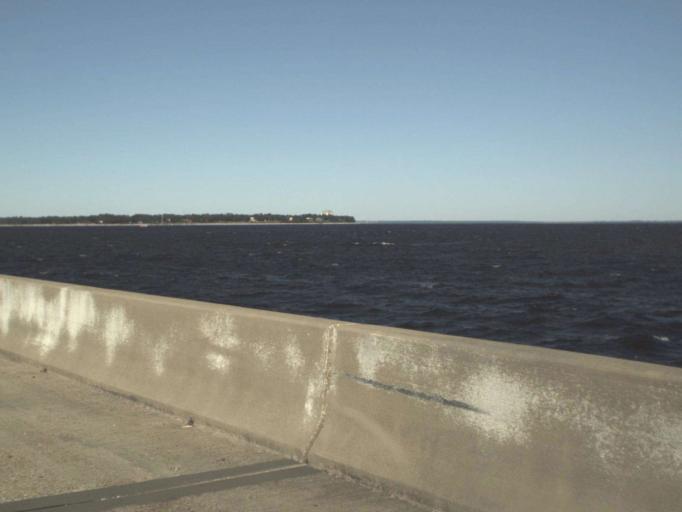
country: US
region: Florida
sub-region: Escambia County
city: East Pensacola Heights
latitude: 30.3994
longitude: -87.1867
